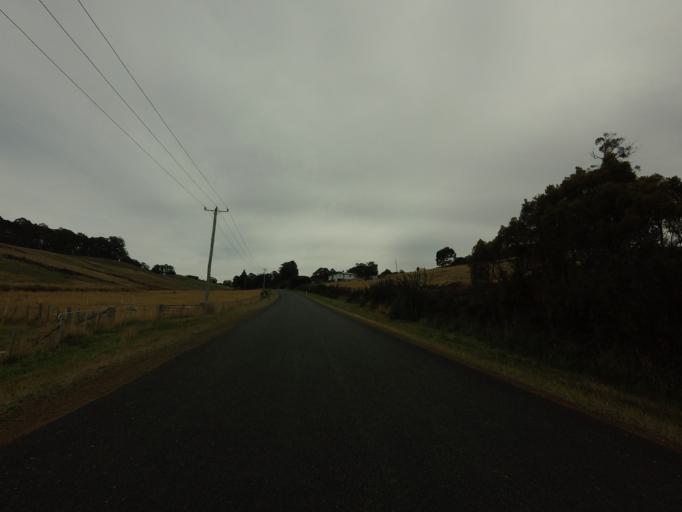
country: AU
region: Tasmania
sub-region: Sorell
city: Sorell
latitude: -42.5363
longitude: 147.5684
